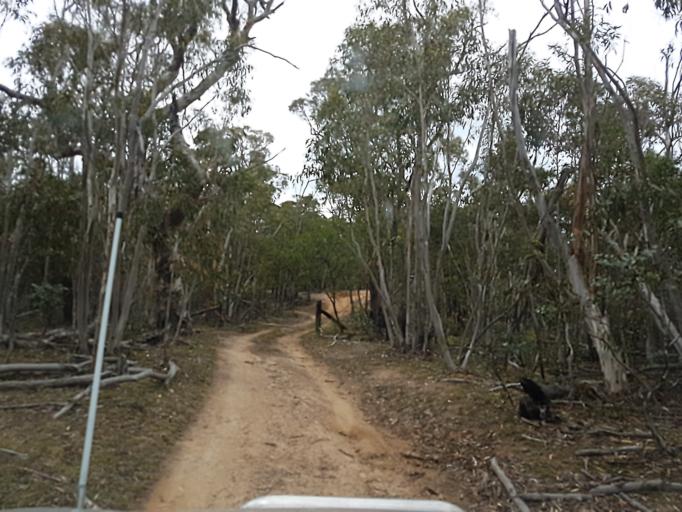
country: AU
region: New South Wales
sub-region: Snowy River
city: Jindabyne
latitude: -36.8615
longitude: 148.2649
